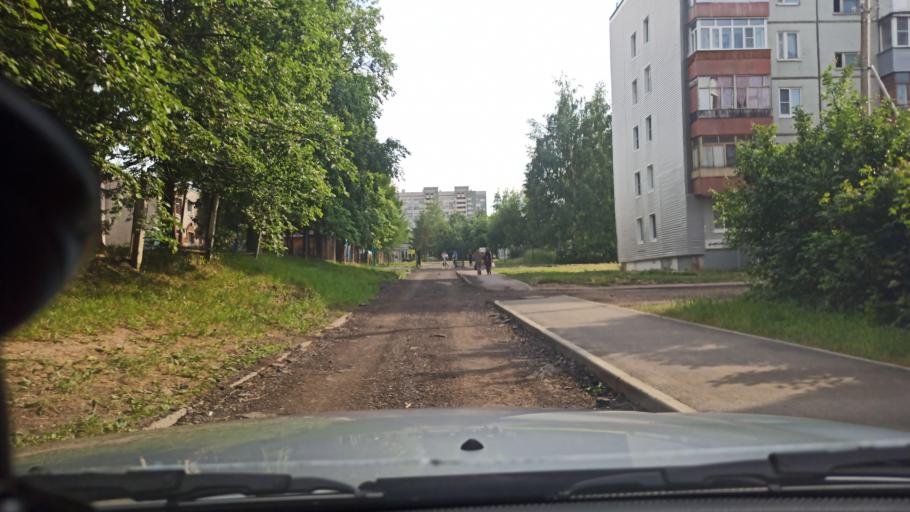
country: RU
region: Vologda
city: Vologda
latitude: 59.1865
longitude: 39.9072
